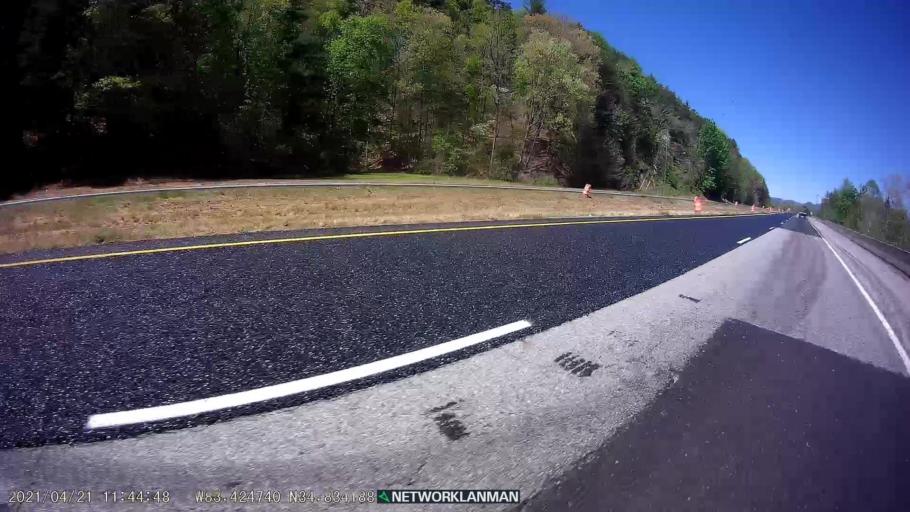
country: US
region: Georgia
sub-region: Rabun County
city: Clayton
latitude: 34.8338
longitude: -83.4245
